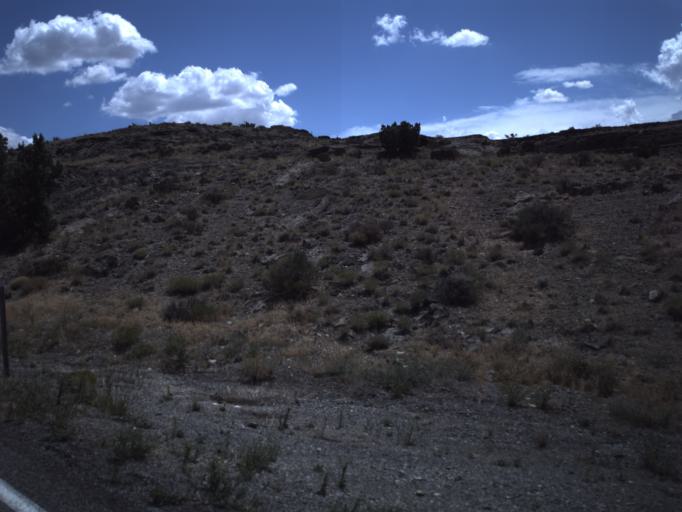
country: US
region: Utah
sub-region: Beaver County
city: Milford
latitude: 39.0791
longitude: -113.6985
